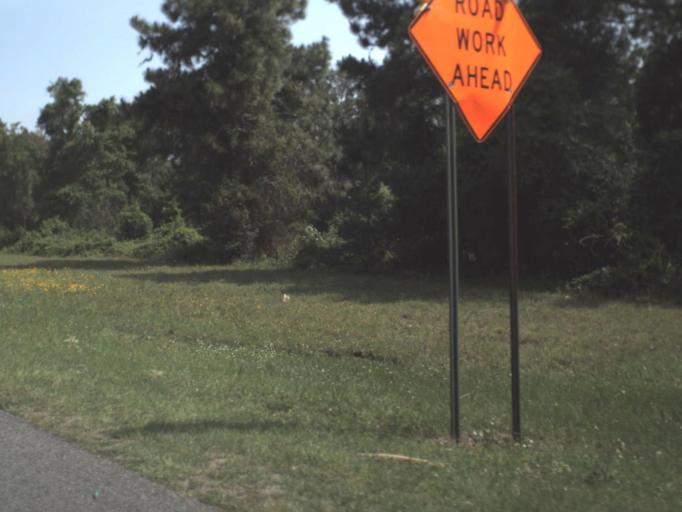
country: US
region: Florida
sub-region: Saint Johns County
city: Palm Valley
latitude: 30.0949
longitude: -81.4690
